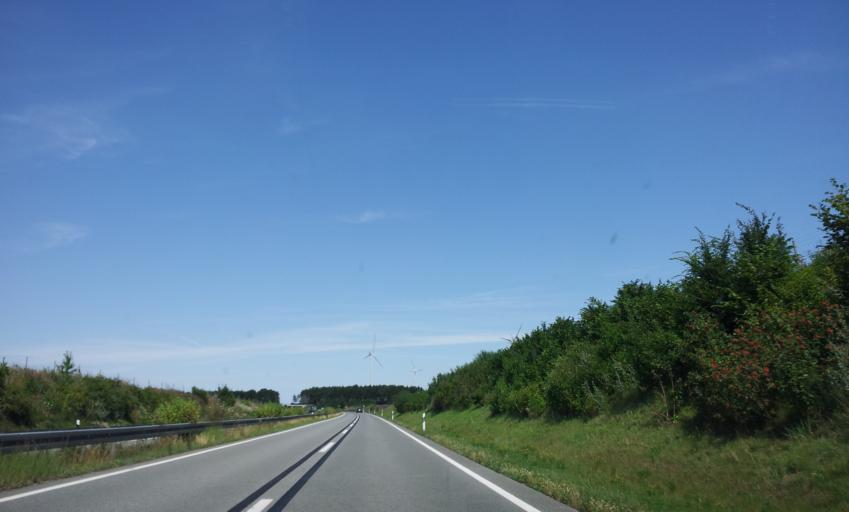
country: DE
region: Mecklenburg-Vorpommern
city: Brandshagen
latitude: 54.1525
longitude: 13.1692
